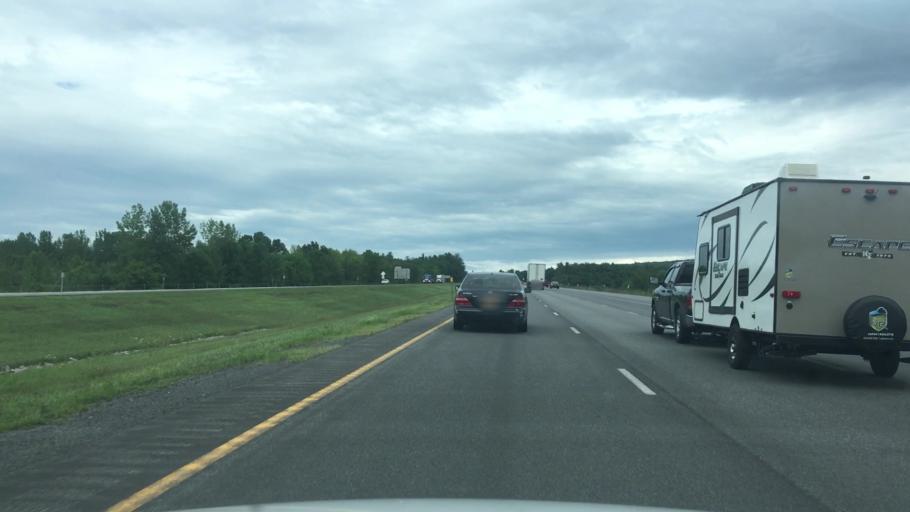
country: US
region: New York
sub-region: Schoharie County
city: Schoharie
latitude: 42.7075
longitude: -74.3102
